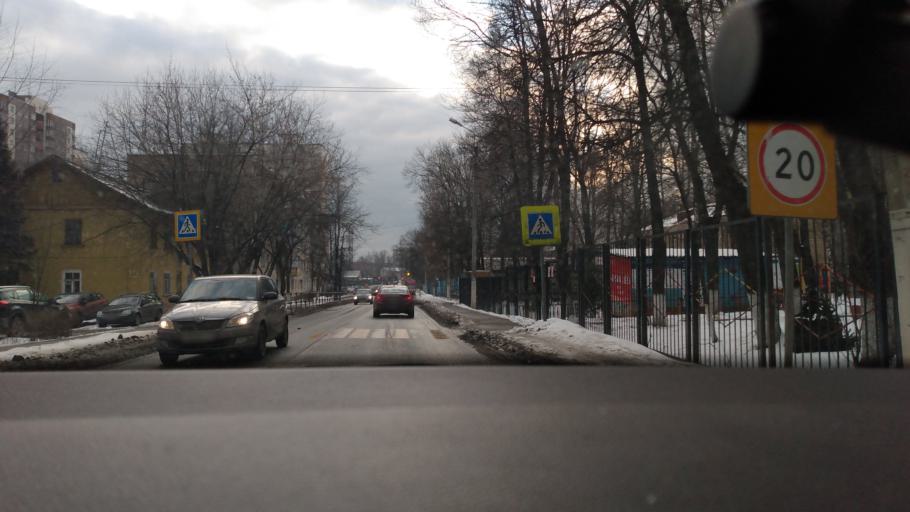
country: RU
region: Moskovskaya
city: Zheleznodorozhnyy
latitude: 55.7316
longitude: 38.0323
